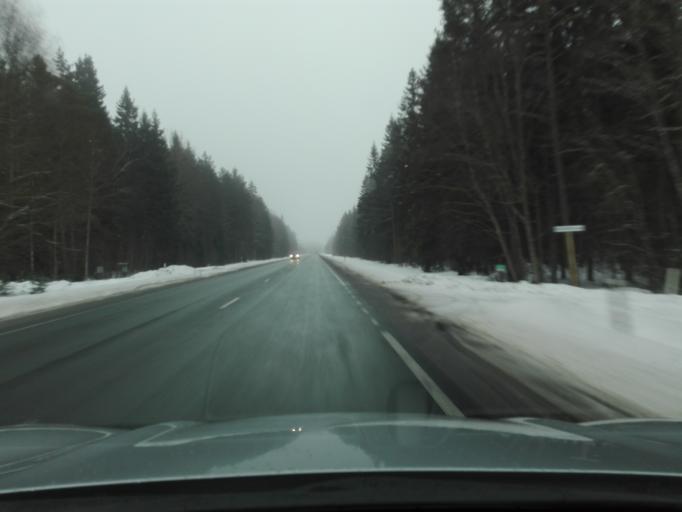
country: EE
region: Raplamaa
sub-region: Kohila vald
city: Kohila
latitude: 59.1491
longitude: 24.7832
